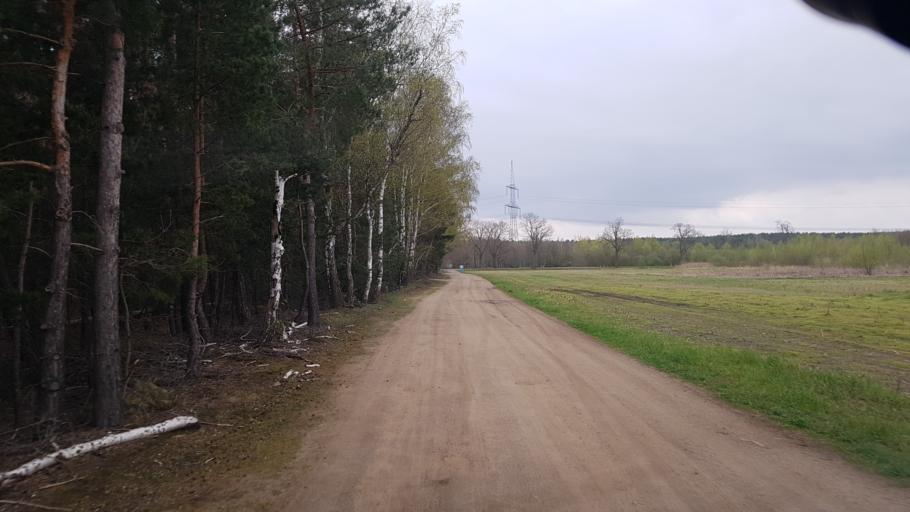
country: DE
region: Brandenburg
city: Altdobern
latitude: 51.6803
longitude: 14.0570
